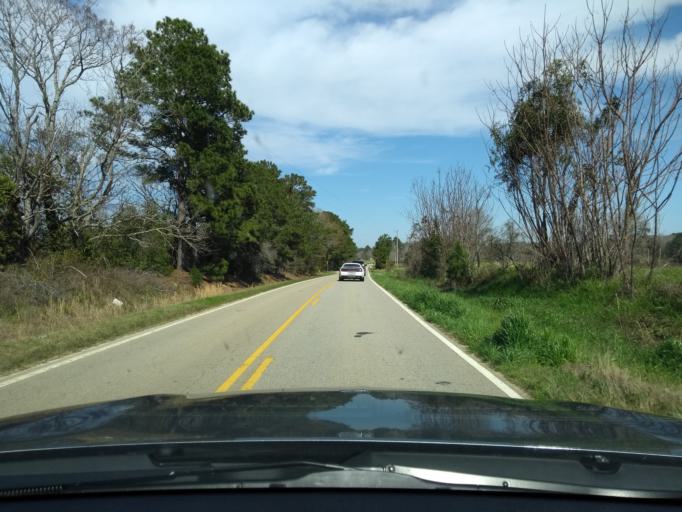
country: US
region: Georgia
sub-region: Bulloch County
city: Brooklet
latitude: 32.4667
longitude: -81.6463
